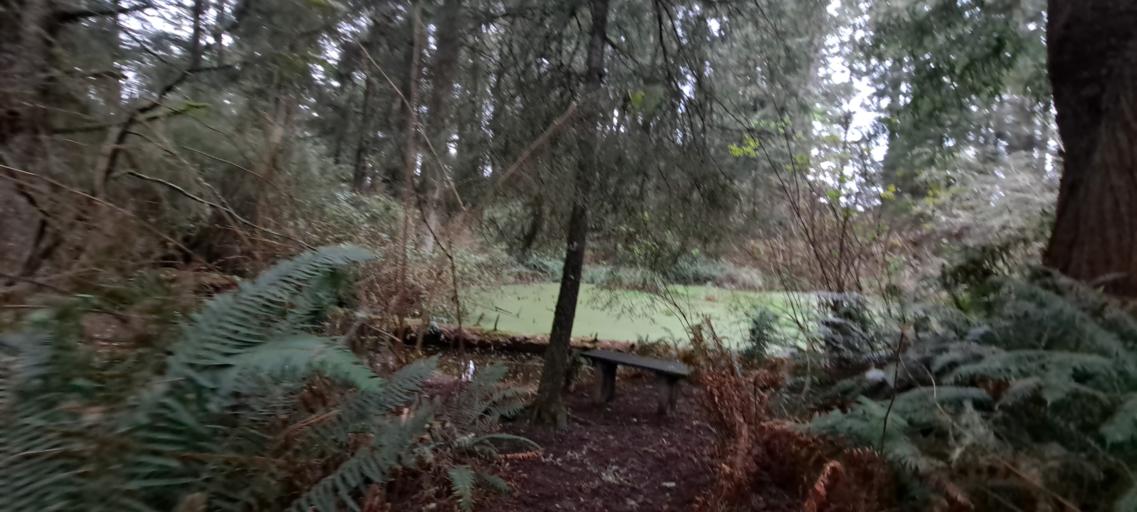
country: US
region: California
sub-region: Humboldt County
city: Ferndale
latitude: 40.5675
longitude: -124.2563
